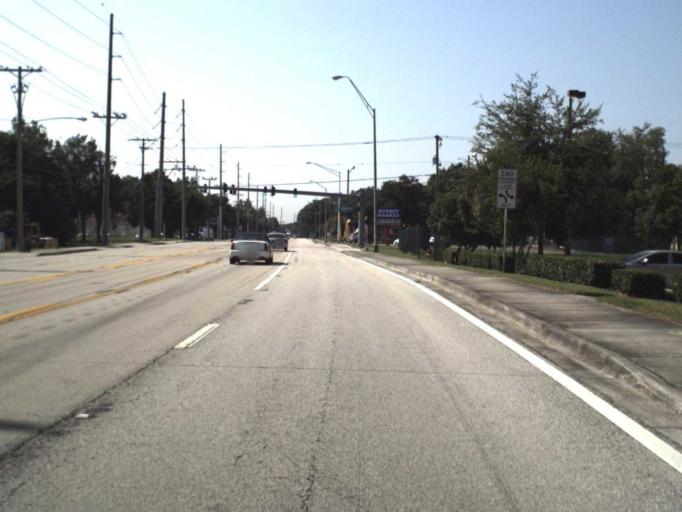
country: US
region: Florida
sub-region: Hillsborough County
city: Lake Magdalene
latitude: 28.0962
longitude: -82.4614
